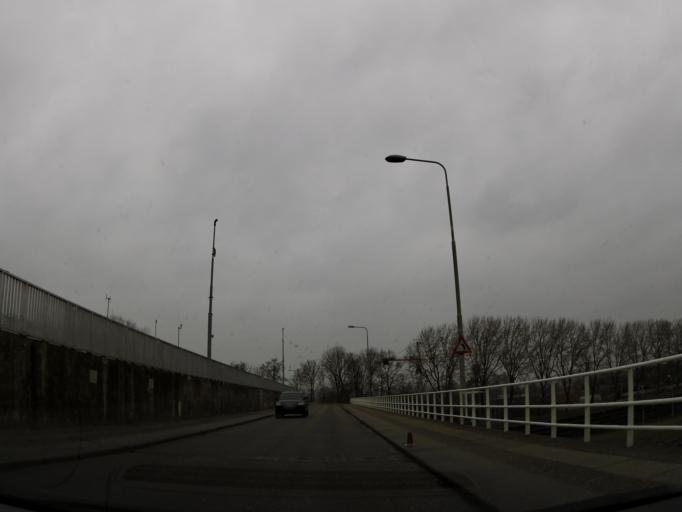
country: NL
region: Limburg
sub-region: Gemeente Maasgouw
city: Maasbracht
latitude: 51.1422
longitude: 5.8791
